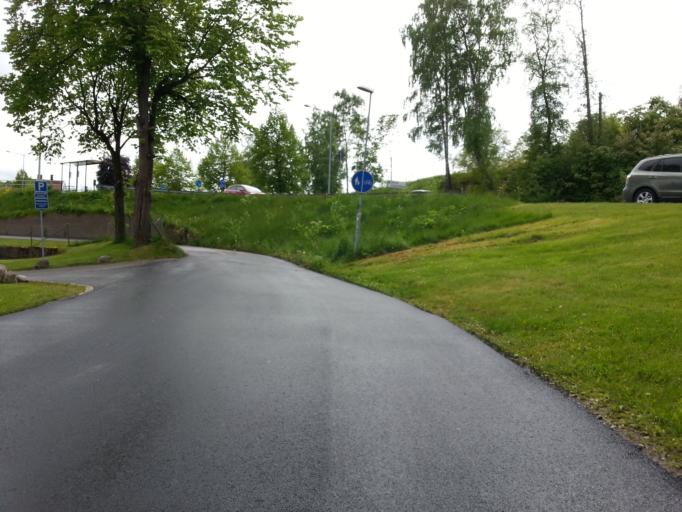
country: SE
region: Joenkoeping
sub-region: Jonkopings Kommun
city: Jonkoping
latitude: 57.7877
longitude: 14.1505
